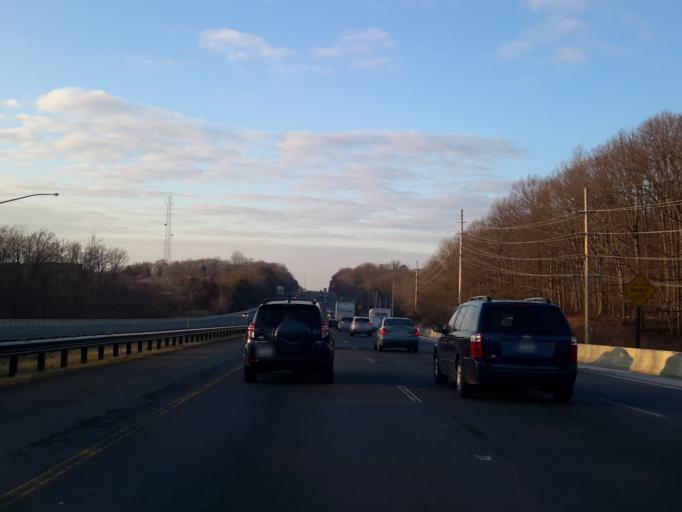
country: US
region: Maryland
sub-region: Montgomery County
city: Clarksburg
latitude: 39.2352
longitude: -77.2875
